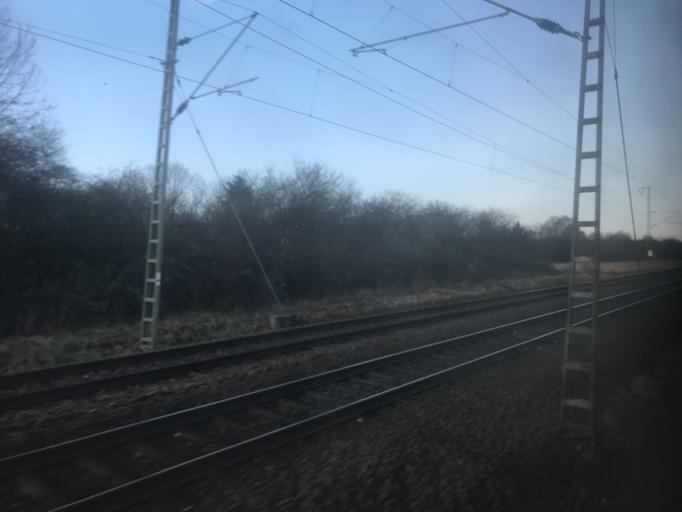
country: DE
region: North Rhine-Westphalia
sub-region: Regierungsbezirk Dusseldorf
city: Langenfeld
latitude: 51.0828
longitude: 6.9506
